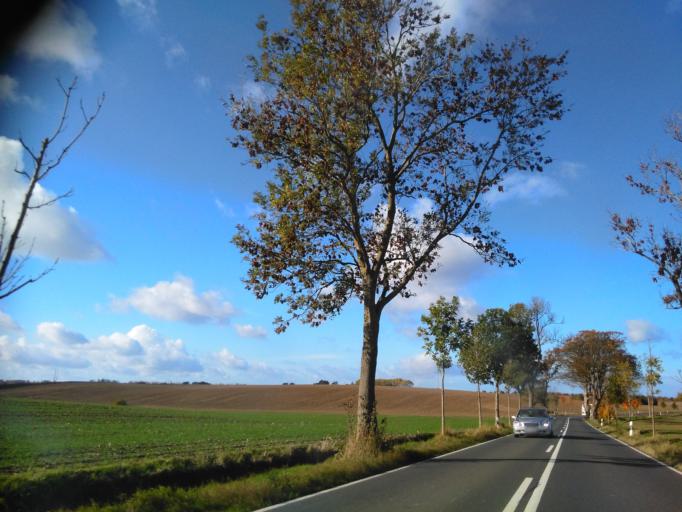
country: DE
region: Mecklenburg-Vorpommern
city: Rambin
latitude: 54.3117
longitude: 13.1777
